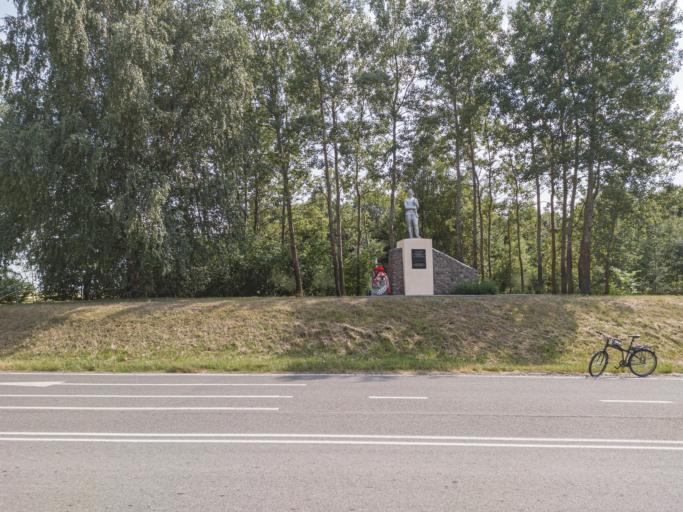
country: BY
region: Brest
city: Kamyanyets
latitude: 52.4006
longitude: 23.8996
